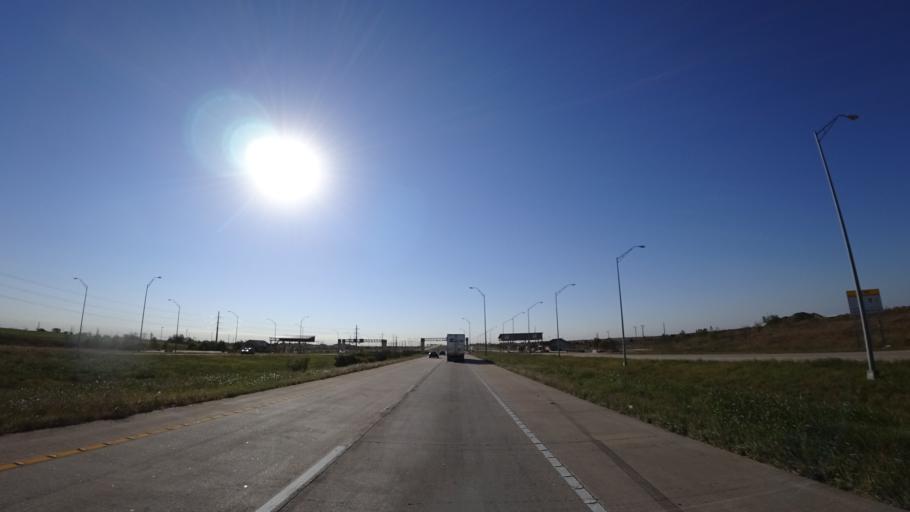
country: US
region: Texas
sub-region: Travis County
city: Pflugerville
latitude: 30.4163
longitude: -97.5864
